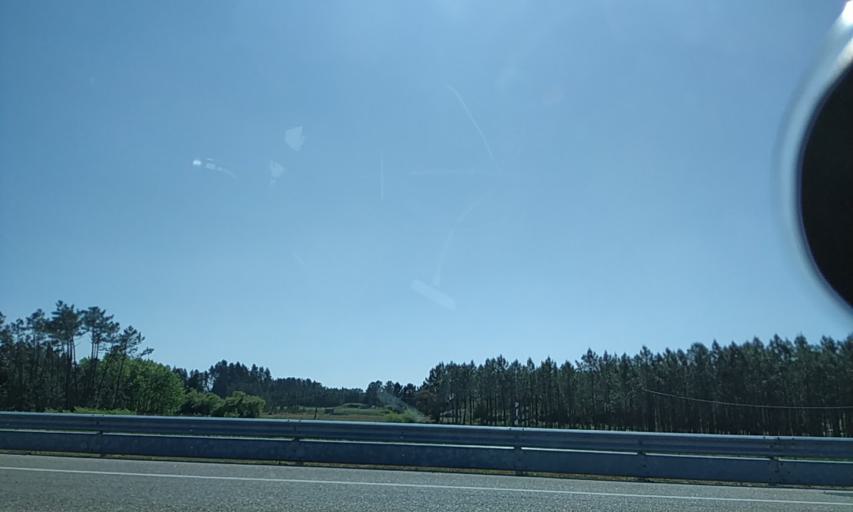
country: PT
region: Coimbra
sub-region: Montemor-O-Velho
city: Arazede
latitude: 40.3253
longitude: -8.7221
